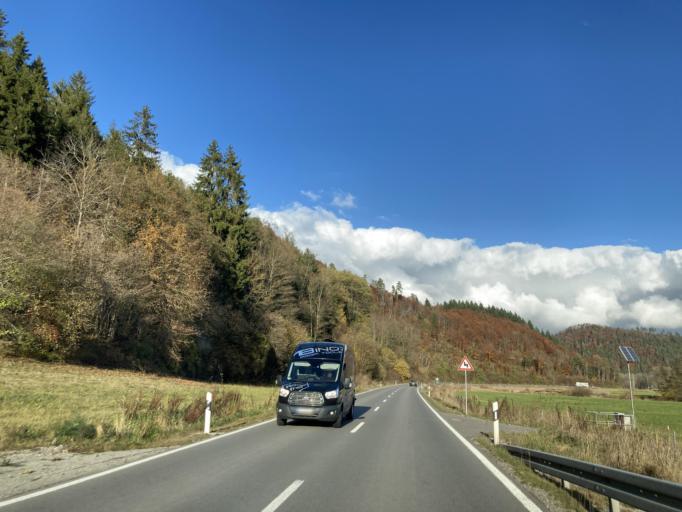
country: DE
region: Baden-Wuerttemberg
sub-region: Freiburg Region
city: Sulz am Neckar
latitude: 48.3917
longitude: 8.6343
